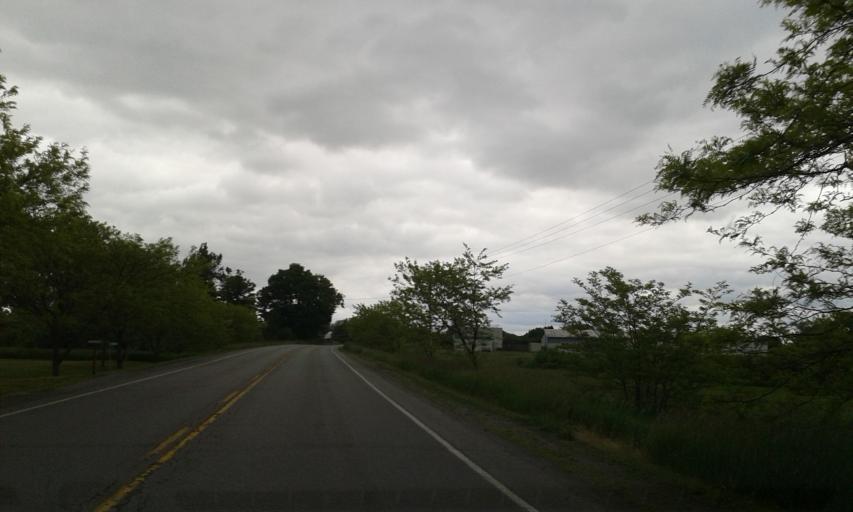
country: CA
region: Ontario
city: Prince Edward
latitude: 43.9443
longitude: -77.3772
